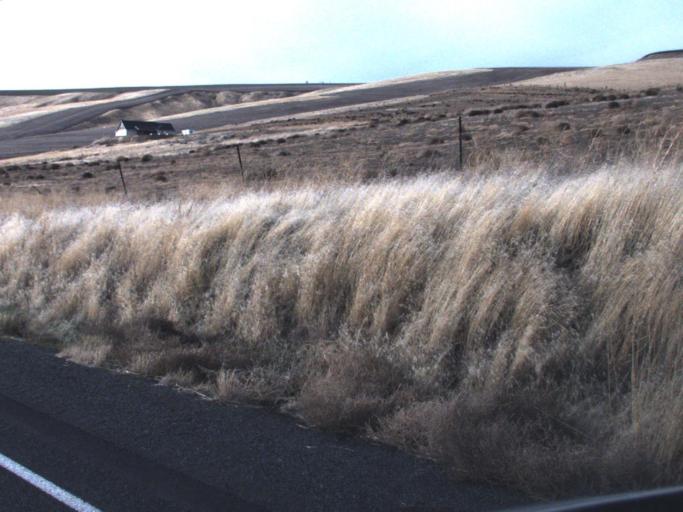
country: US
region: Washington
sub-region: Garfield County
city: Pomeroy
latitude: 46.4760
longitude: -117.6544
